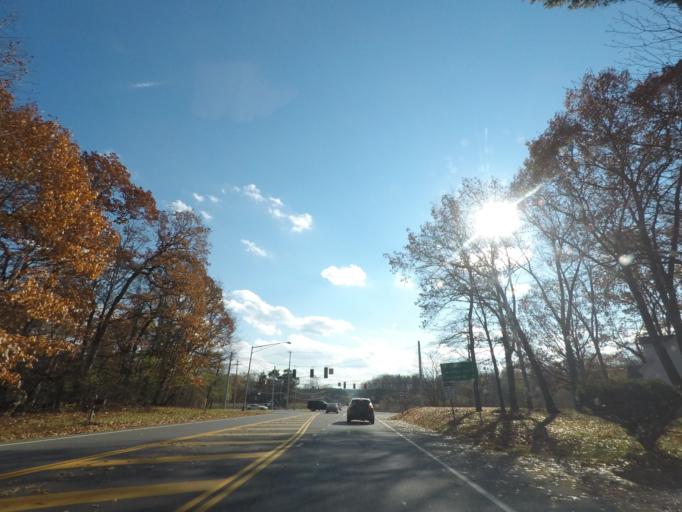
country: US
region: New York
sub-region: Schenectady County
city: East Glenville
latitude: 42.8670
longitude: -73.8880
